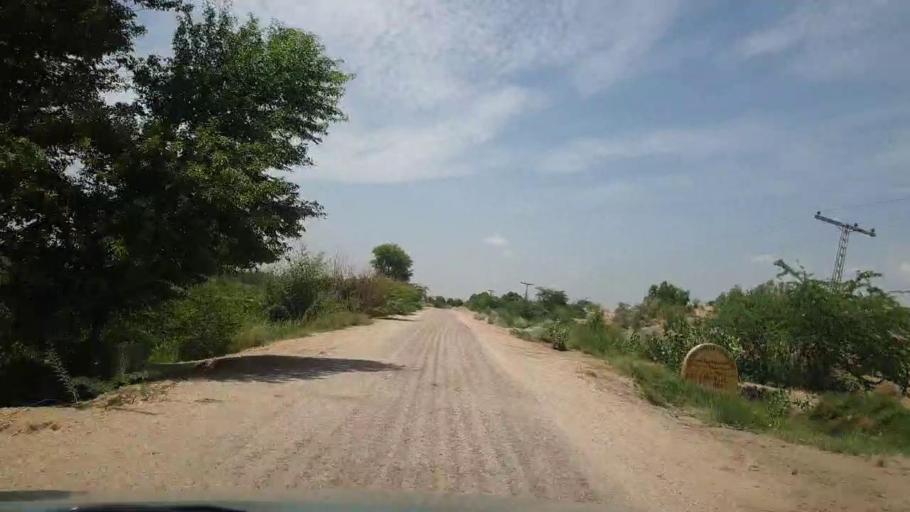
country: PK
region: Sindh
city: Bozdar
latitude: 27.0838
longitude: 68.9821
